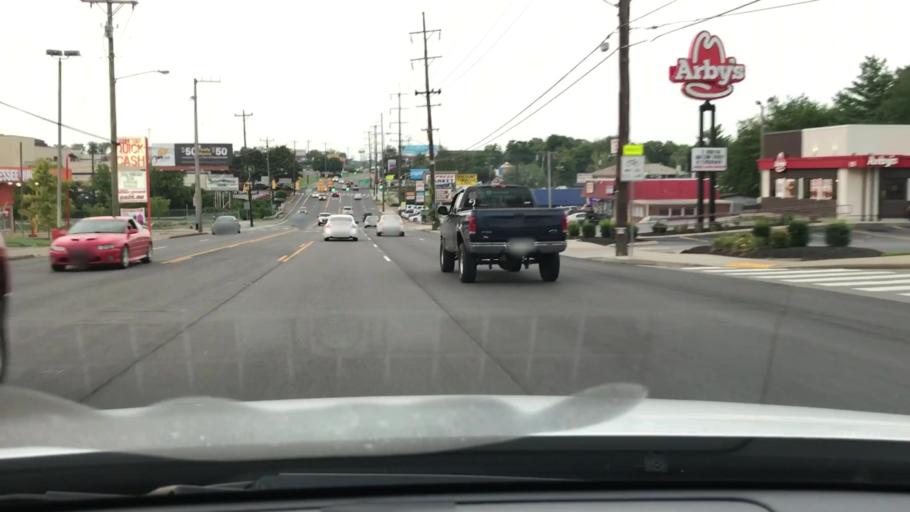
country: US
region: Tennessee
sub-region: Davidson County
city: Goodlettsville
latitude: 36.2511
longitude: -86.7182
